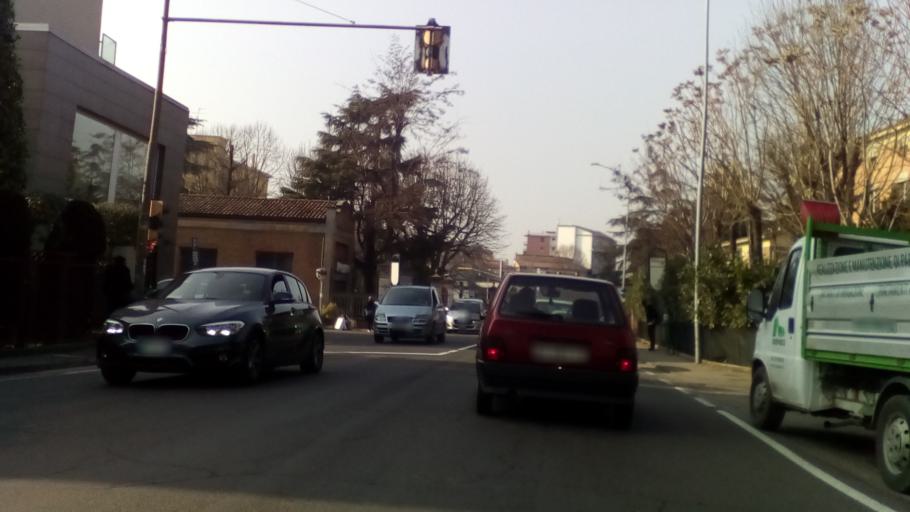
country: IT
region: Emilia-Romagna
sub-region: Provincia di Modena
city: Modena
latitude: 44.6334
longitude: 10.9379
